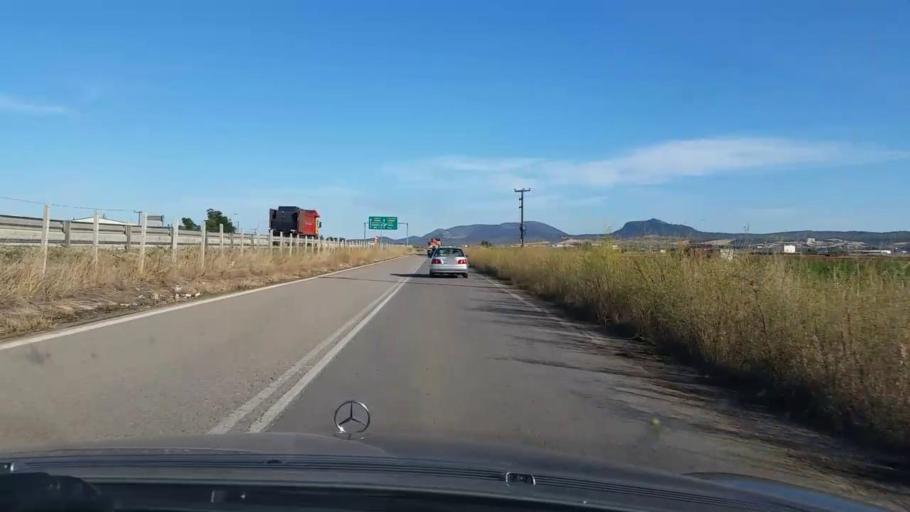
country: GR
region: Central Greece
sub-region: Nomos Voiotias
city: Thivai
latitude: 38.3652
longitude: 23.3103
